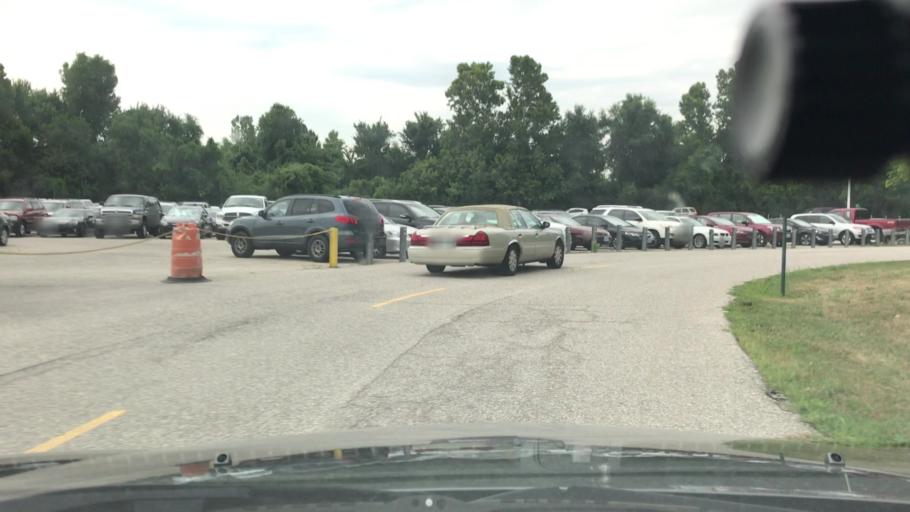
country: US
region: Missouri
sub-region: Saint Charles County
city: Saint Charles
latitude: 38.7462
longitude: -90.5107
